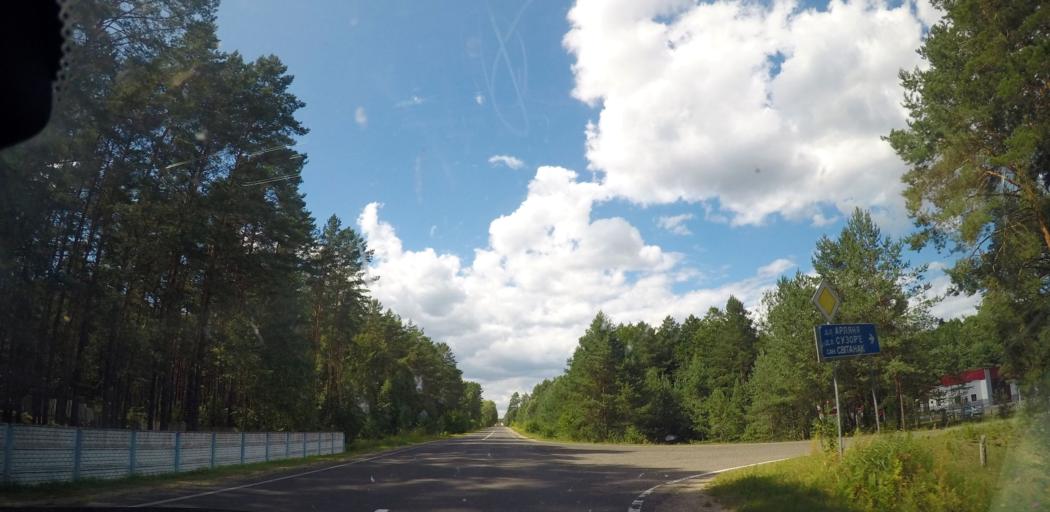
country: LT
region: Alytaus apskritis
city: Druskininkai
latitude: 53.8766
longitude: 24.1480
